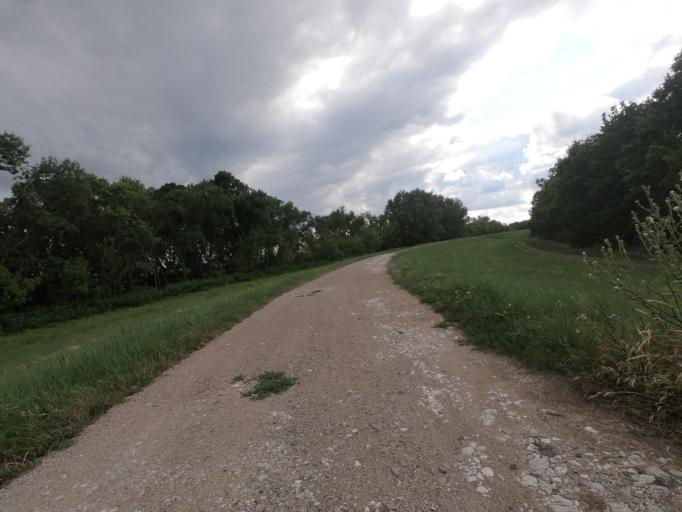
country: HU
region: Heves
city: Poroszlo
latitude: 47.6743
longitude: 20.7093
